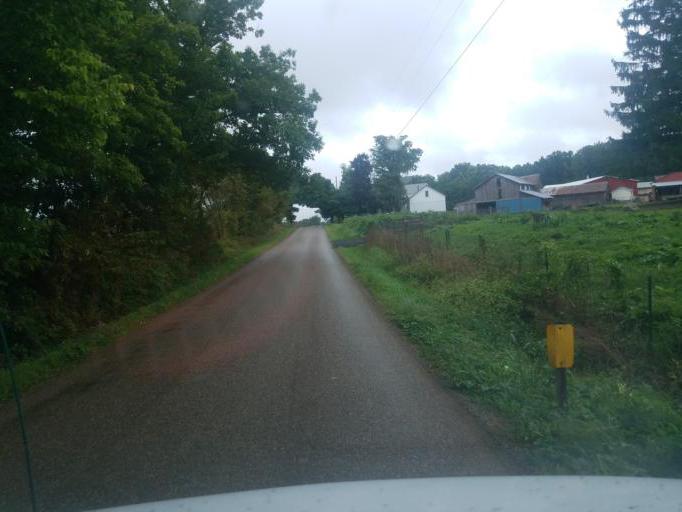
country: US
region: Ohio
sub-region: Wayne County
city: West Salem
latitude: 40.9462
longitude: -82.1010
